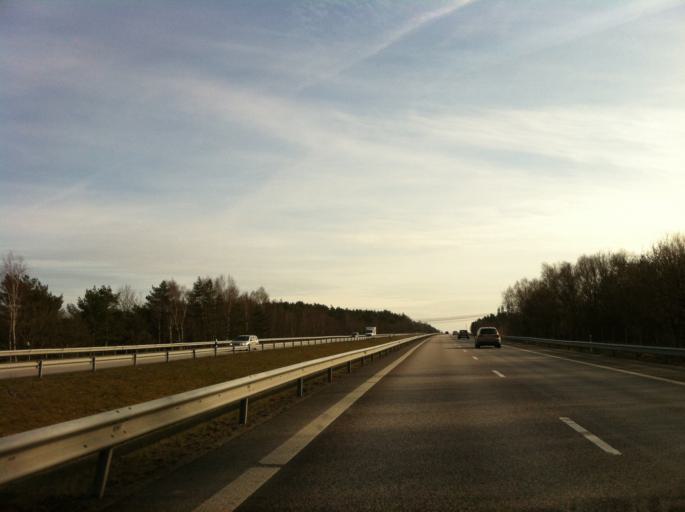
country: SE
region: Halland
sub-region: Kungsbacka Kommun
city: Kungsbacka
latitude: 57.4420
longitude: 12.1160
